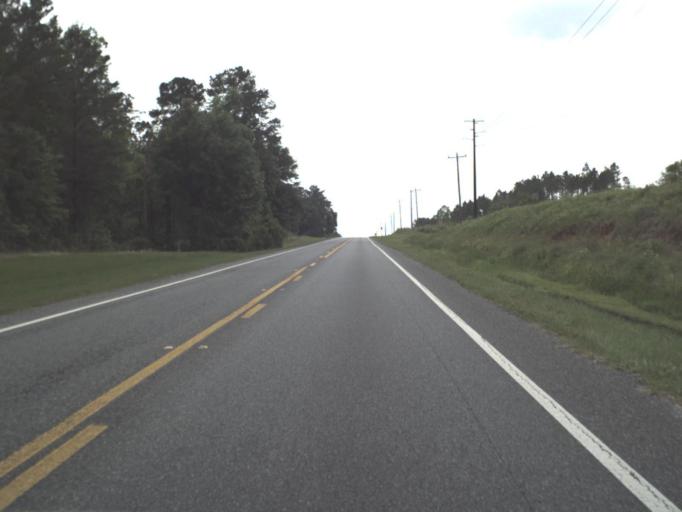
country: US
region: Florida
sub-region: Clay County
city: Middleburg
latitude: 30.0216
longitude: -81.8976
